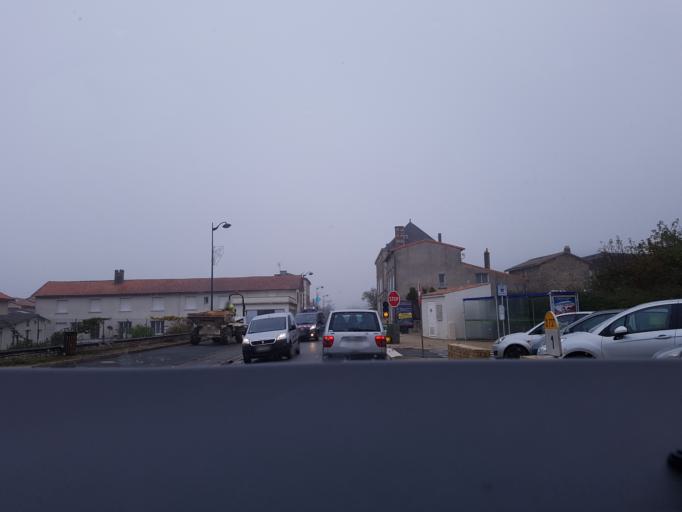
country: FR
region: Poitou-Charentes
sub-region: Departement des Deux-Sevres
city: Nanteuil
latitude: 46.4117
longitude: -0.1748
